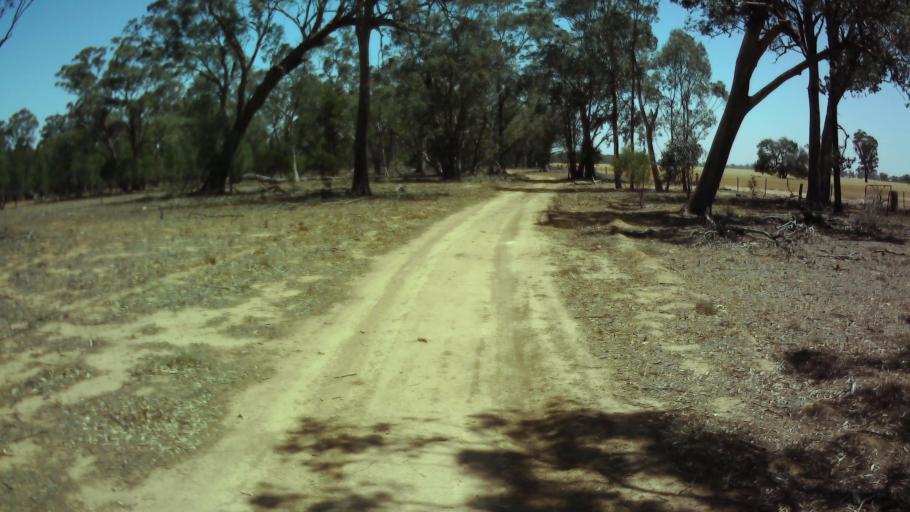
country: AU
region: New South Wales
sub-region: Weddin
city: Grenfell
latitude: -34.0629
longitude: 147.8061
